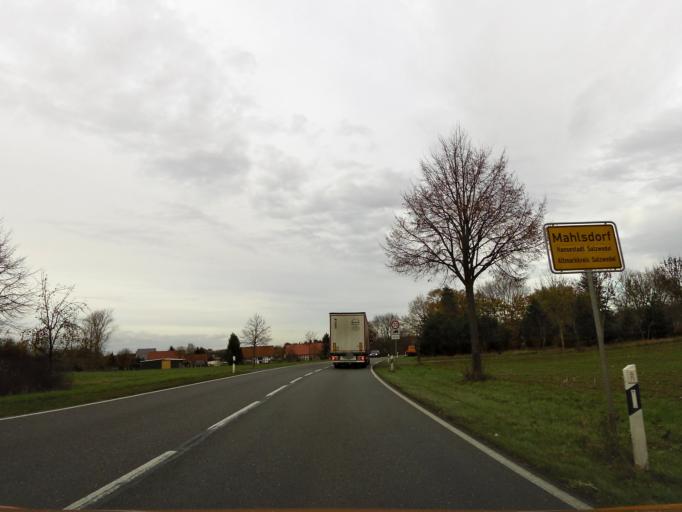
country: DE
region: Saxony-Anhalt
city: Pretzier
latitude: 52.7890
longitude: 11.2318
